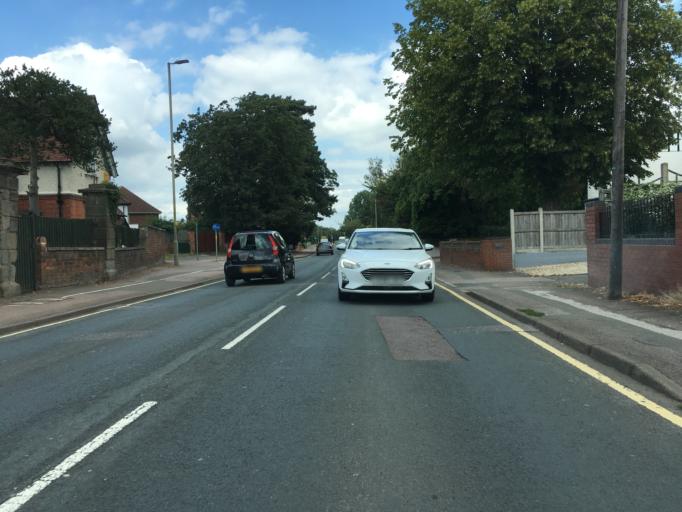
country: GB
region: England
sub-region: Gloucestershire
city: Gloucester
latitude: 51.8787
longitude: -2.2401
